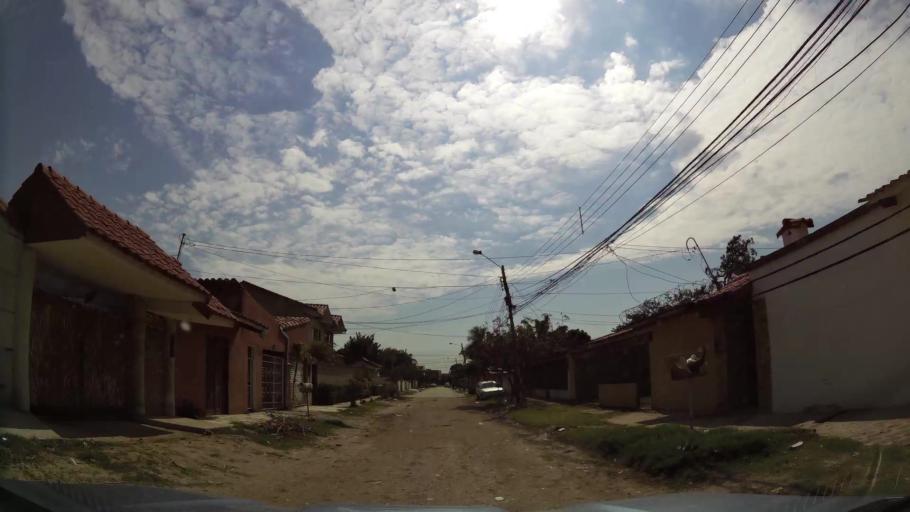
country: BO
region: Santa Cruz
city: Santa Cruz de la Sierra
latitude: -17.7480
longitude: -63.1577
